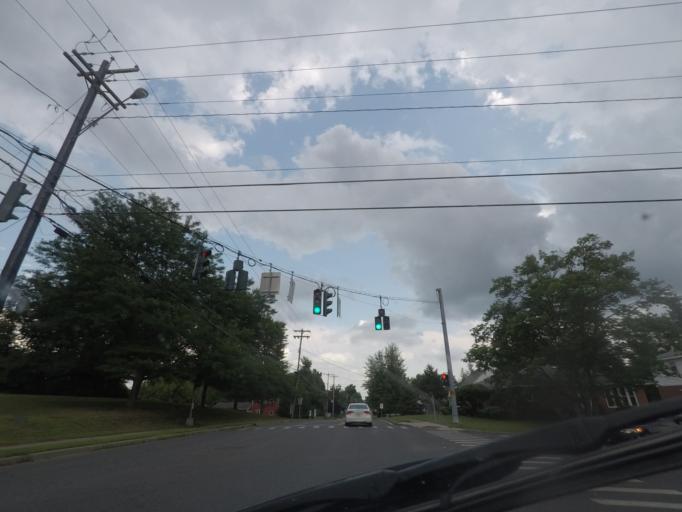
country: US
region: New York
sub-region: Albany County
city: Roessleville
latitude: 42.6969
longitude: -73.7909
